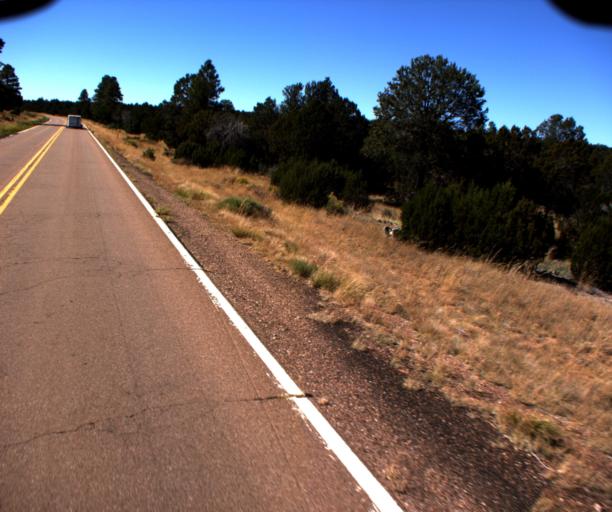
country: US
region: Arizona
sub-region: Navajo County
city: Heber-Overgaard
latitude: 34.4543
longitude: -110.5226
